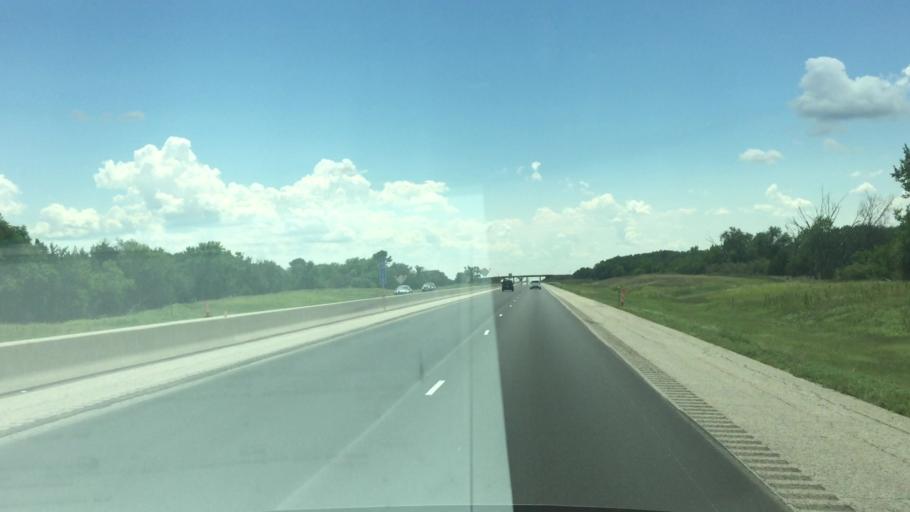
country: US
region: Kansas
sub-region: Osage County
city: Osage City
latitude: 38.7032
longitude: -95.9875
